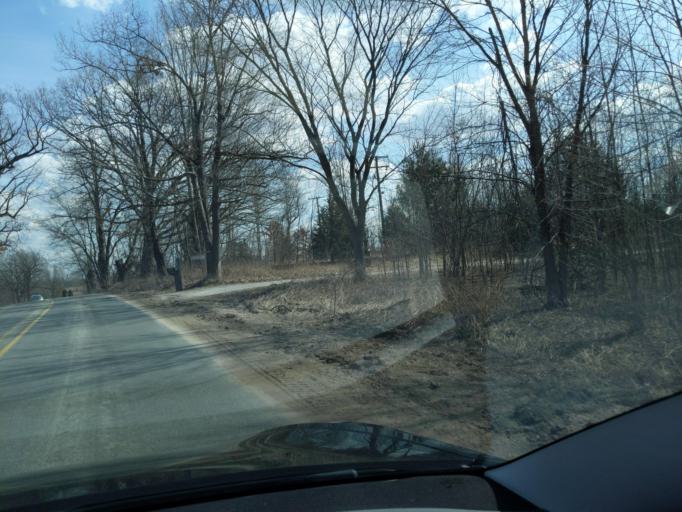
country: US
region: Michigan
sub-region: Livingston County
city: Pinckney
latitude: 42.3918
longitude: -83.9563
